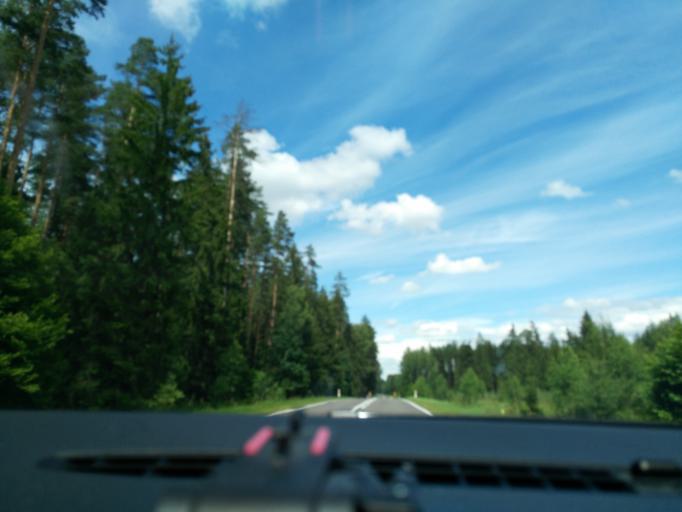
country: PL
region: Podlasie
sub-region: Powiat sejnenski
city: Sejny
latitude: 53.9929
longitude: 23.3068
